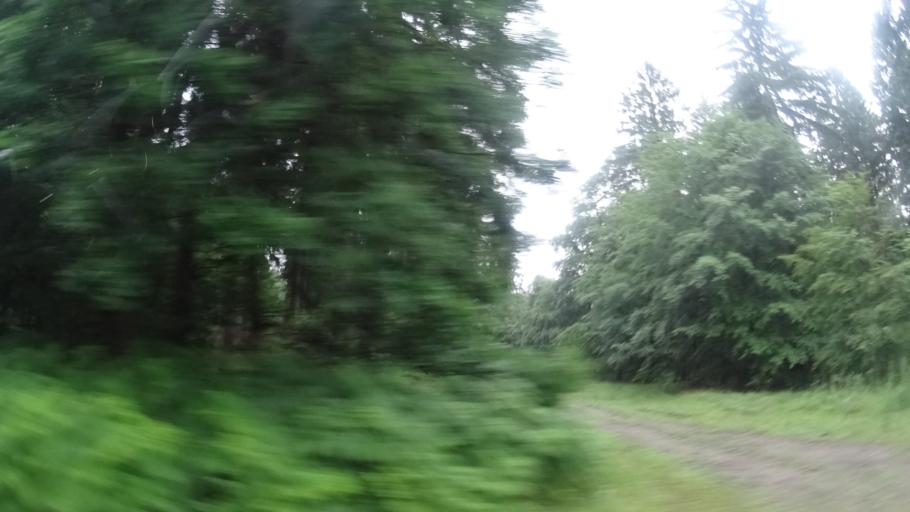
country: BE
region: Wallonia
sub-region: Province du Luxembourg
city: Habay-la-Vieille
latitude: 49.7539
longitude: 5.6003
